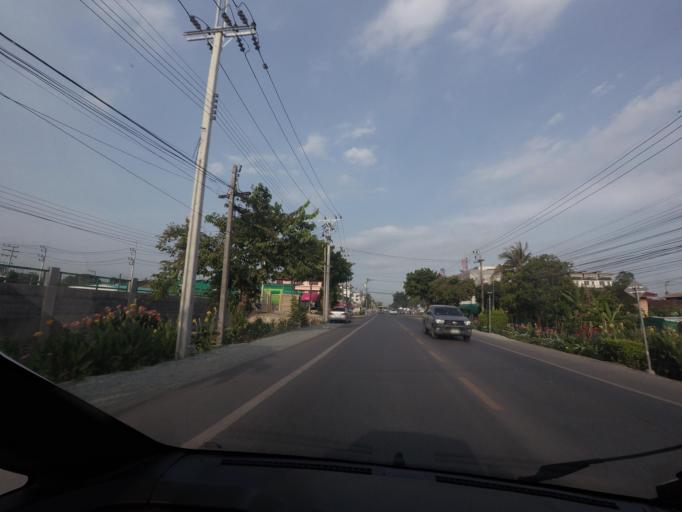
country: TH
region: Bangkok
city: Nong Chok
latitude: 13.8518
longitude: 100.8778
